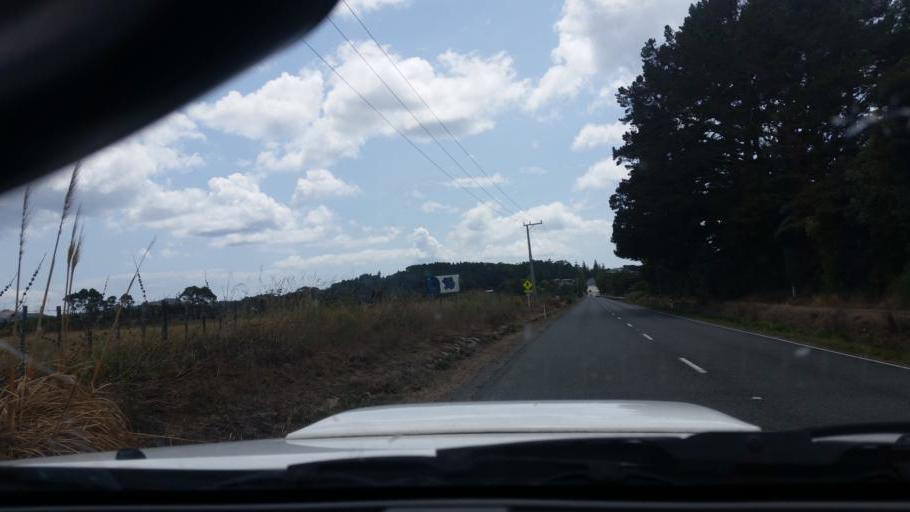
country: NZ
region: Auckland
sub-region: Auckland
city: Wellsford
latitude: -36.1113
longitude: 174.5760
